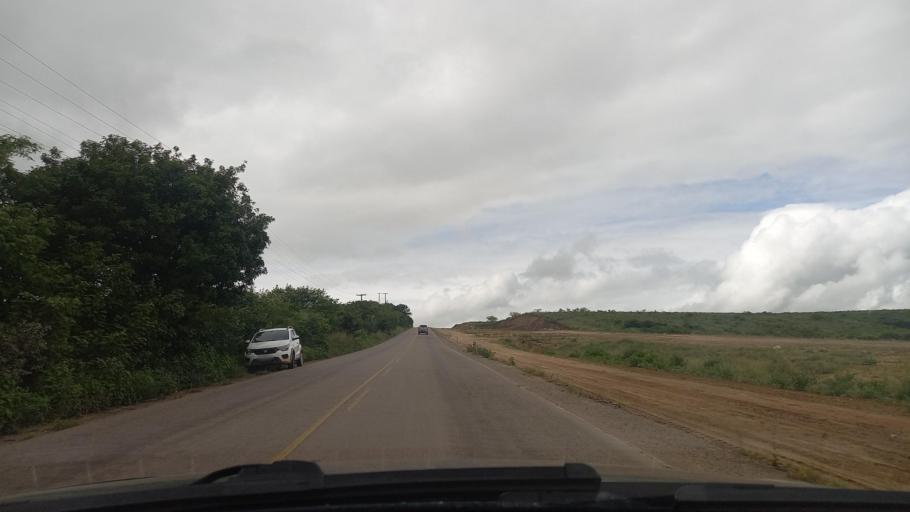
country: BR
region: Alagoas
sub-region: Batalha
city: Batalha
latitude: -9.6384
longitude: -37.1962
